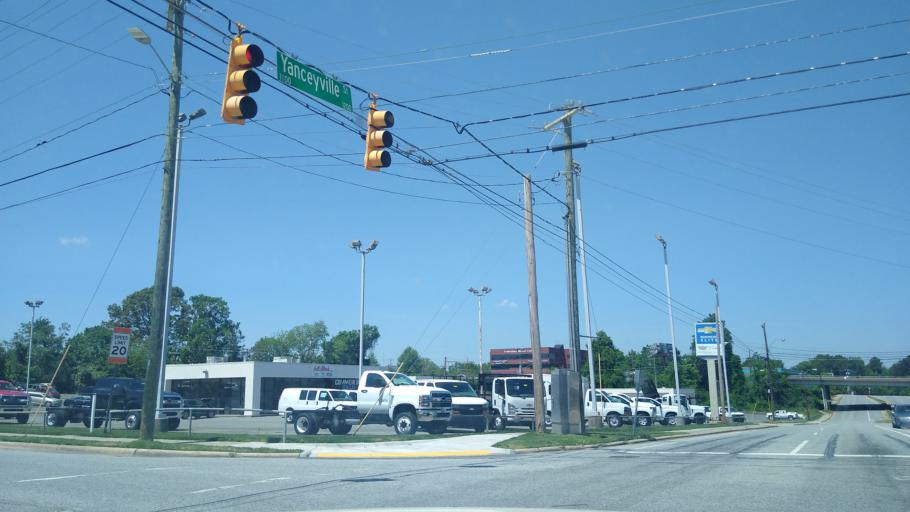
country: US
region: North Carolina
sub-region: Guilford County
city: Greensboro
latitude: 36.0857
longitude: -79.7827
